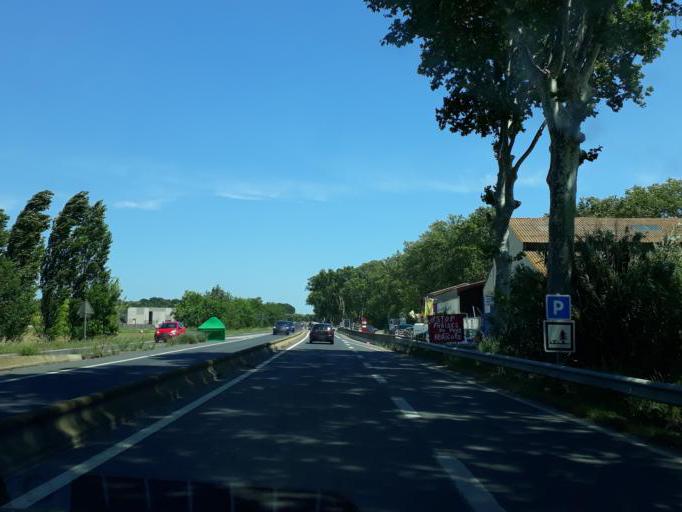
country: FR
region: Languedoc-Roussillon
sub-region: Departement de l'Herault
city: Cers
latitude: 43.3178
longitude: 3.3031
